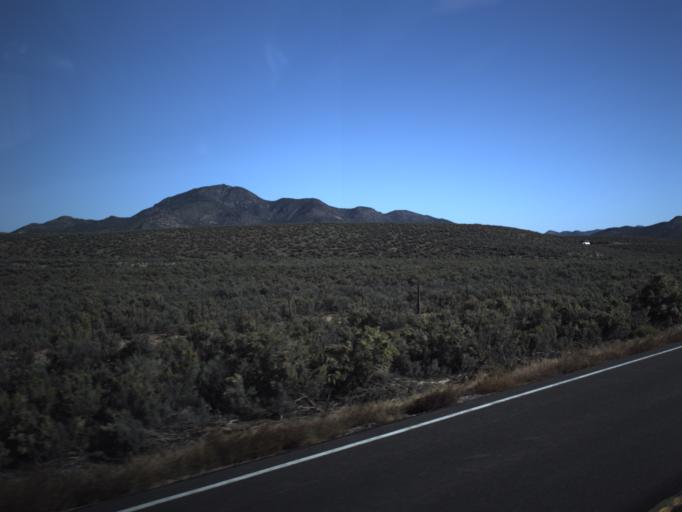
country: US
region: Utah
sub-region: Washington County
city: Enterprise
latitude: 37.7660
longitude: -113.9824
